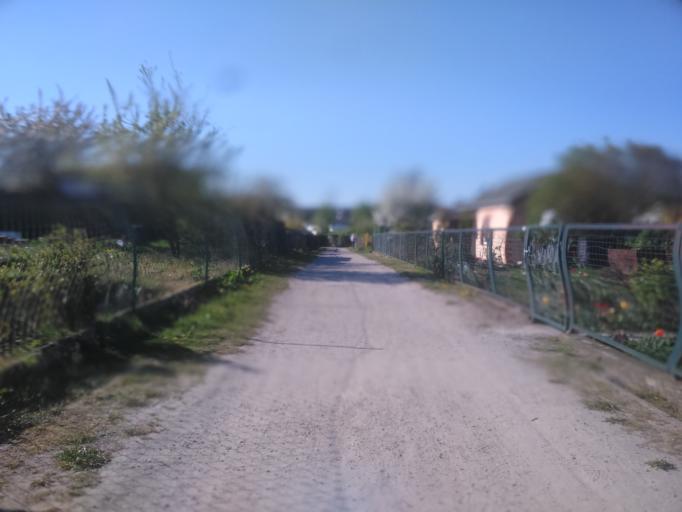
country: DE
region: Berlin
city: Neu-Hohenschoenhausen
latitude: 52.5573
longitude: 13.5086
